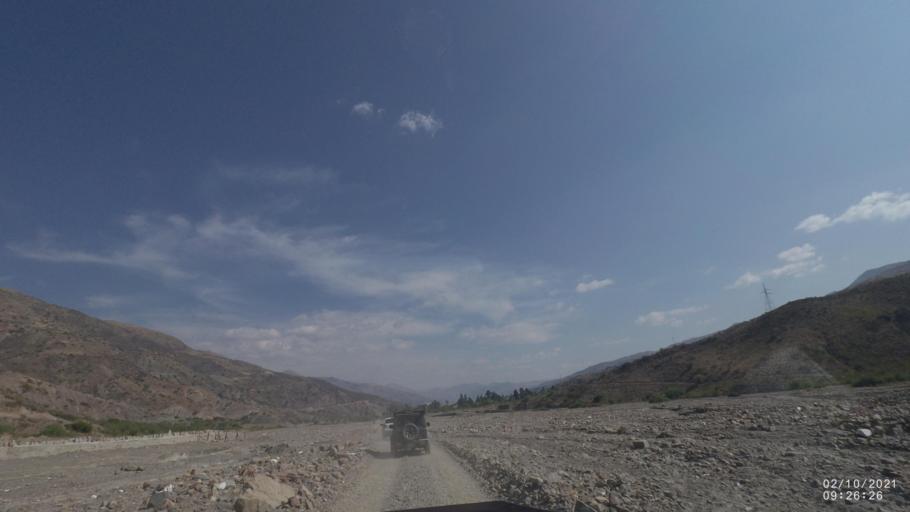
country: BO
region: Cochabamba
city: Irpa Irpa
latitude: -17.8587
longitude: -66.3131
